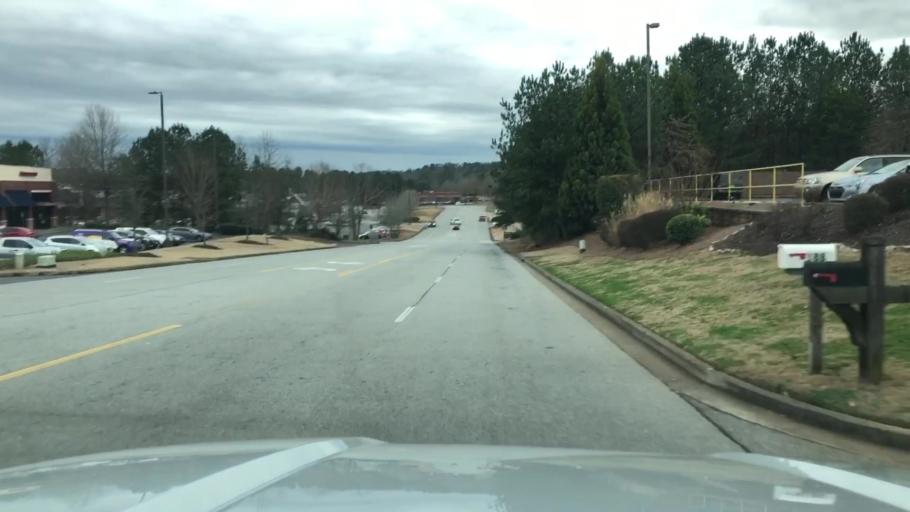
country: US
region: Georgia
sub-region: Cherokee County
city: Woodstock
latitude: 34.0841
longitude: -84.5410
